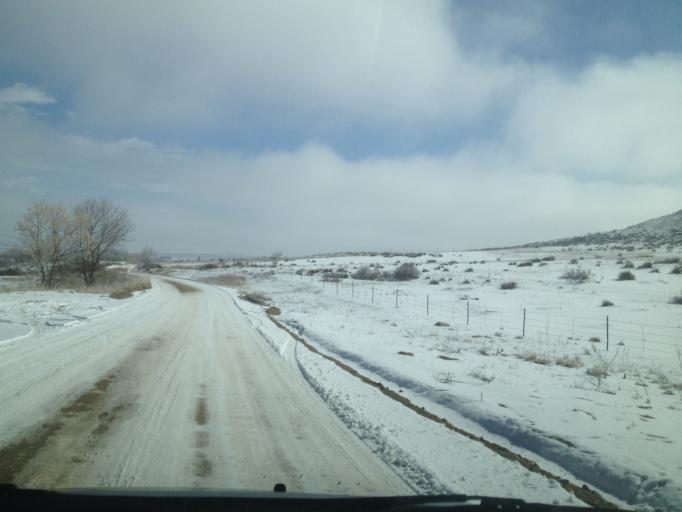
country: US
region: Colorado
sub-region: Boulder County
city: Boulder
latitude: 40.0799
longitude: -105.2690
